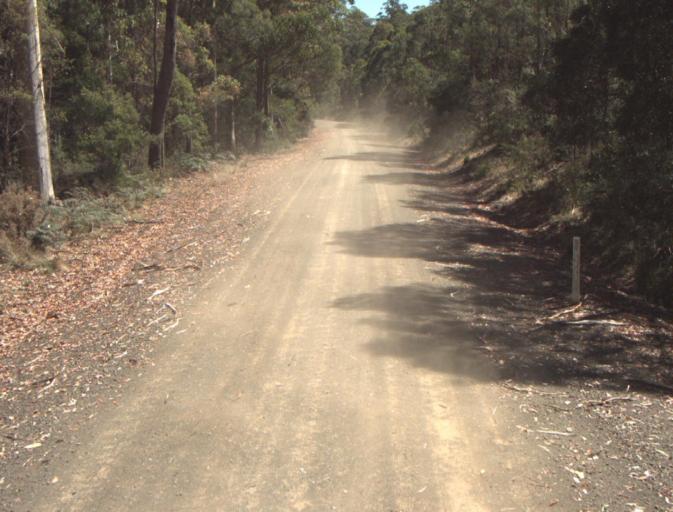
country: AU
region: Tasmania
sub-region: Launceston
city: Newstead
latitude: -41.3067
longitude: 147.3345
